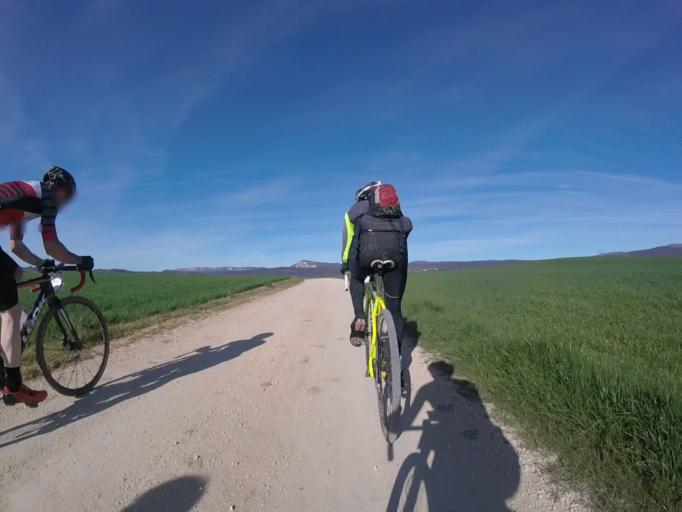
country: ES
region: Navarre
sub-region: Provincia de Navarra
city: Yerri
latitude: 42.7149
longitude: -1.9761
